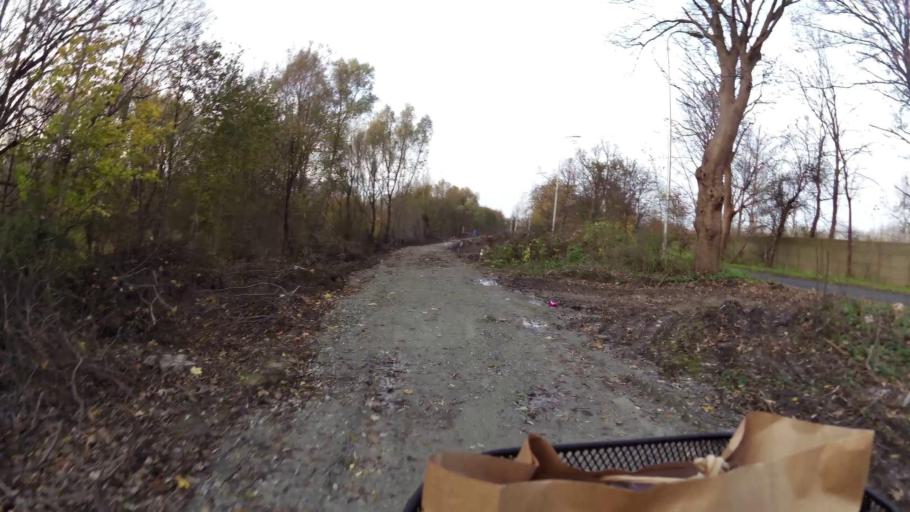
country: PL
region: West Pomeranian Voivodeship
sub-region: Koszalin
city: Koszalin
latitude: 54.2052
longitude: 16.1704
